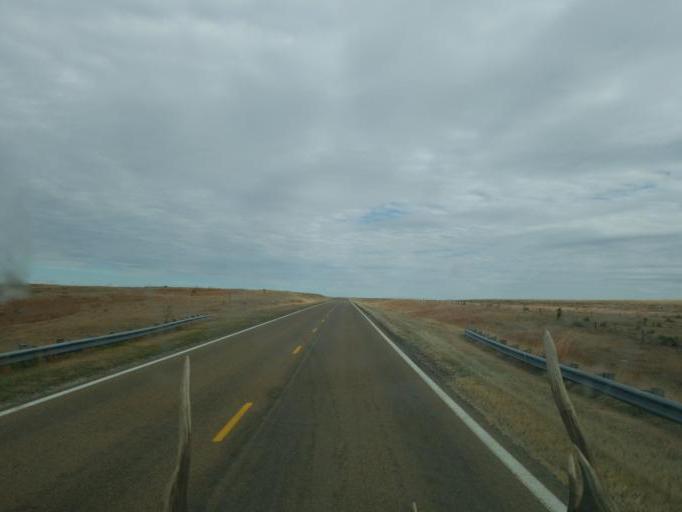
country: US
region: Kansas
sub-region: Thomas County
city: Colby
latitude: 39.0282
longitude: -101.3067
